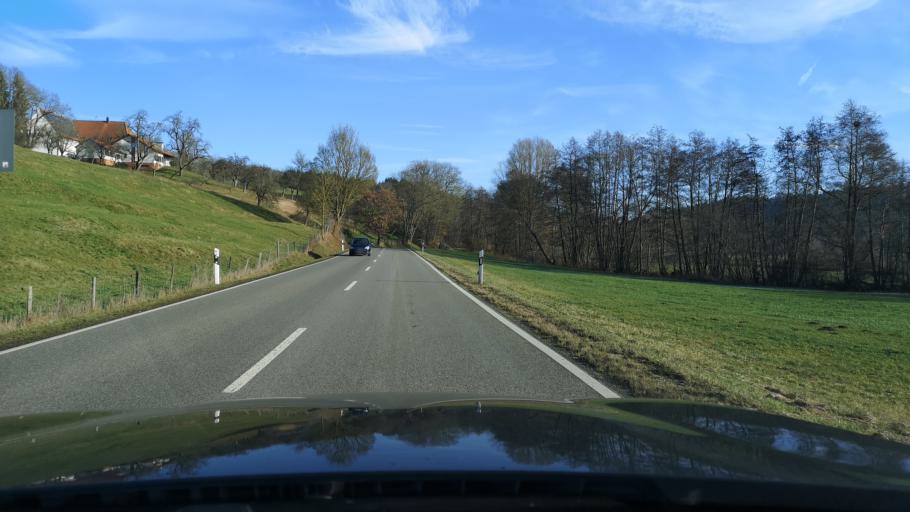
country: DE
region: Baden-Wuerttemberg
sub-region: Regierungsbezirk Stuttgart
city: Neuler
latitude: 48.8956
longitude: 10.0526
